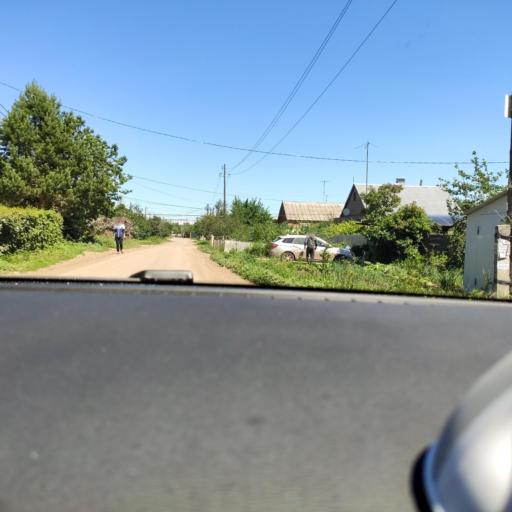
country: RU
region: Samara
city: Petra-Dubrava
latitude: 53.2965
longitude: 50.3082
